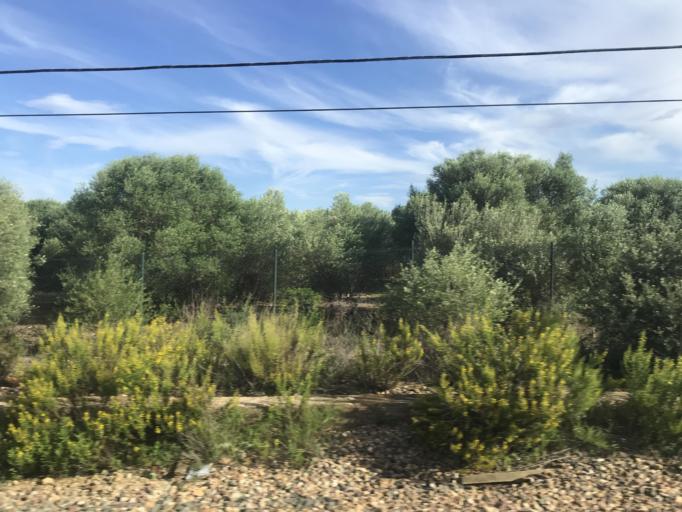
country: ES
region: Valencia
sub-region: Provincia de Castello
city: Vinaros
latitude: 40.4690
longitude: 0.4530
